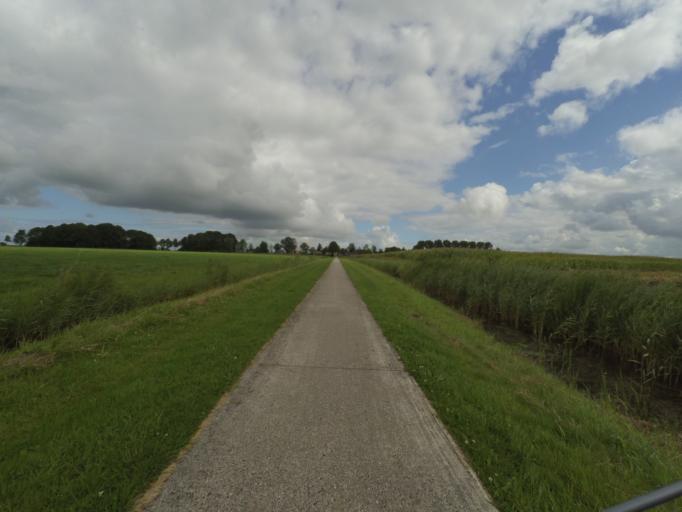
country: NL
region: Friesland
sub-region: Gemeente Kollumerland en Nieuwkruisland
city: Kollum
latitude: 53.2921
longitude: 6.2308
